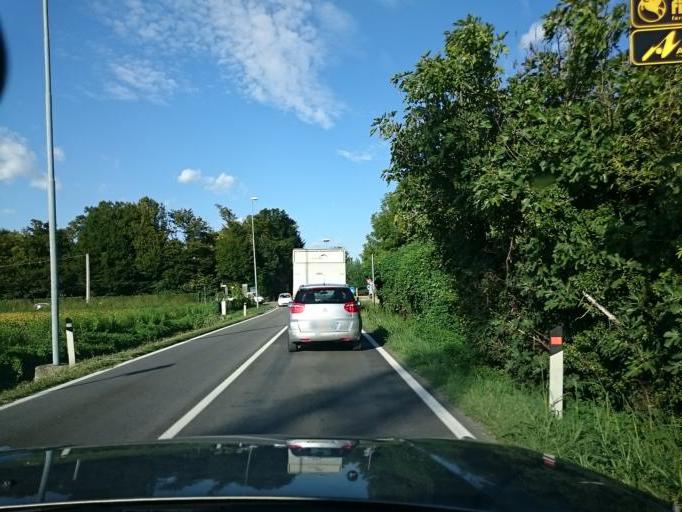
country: IT
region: Veneto
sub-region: Provincia di Padova
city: Abano Terme
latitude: 45.3543
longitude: 11.8079
